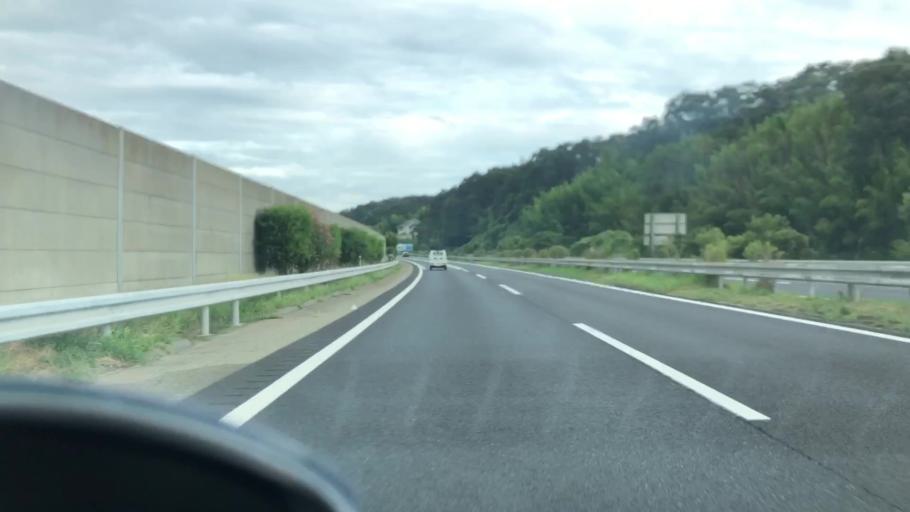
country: JP
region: Hyogo
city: Yashiro
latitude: 34.9012
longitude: 135.0691
